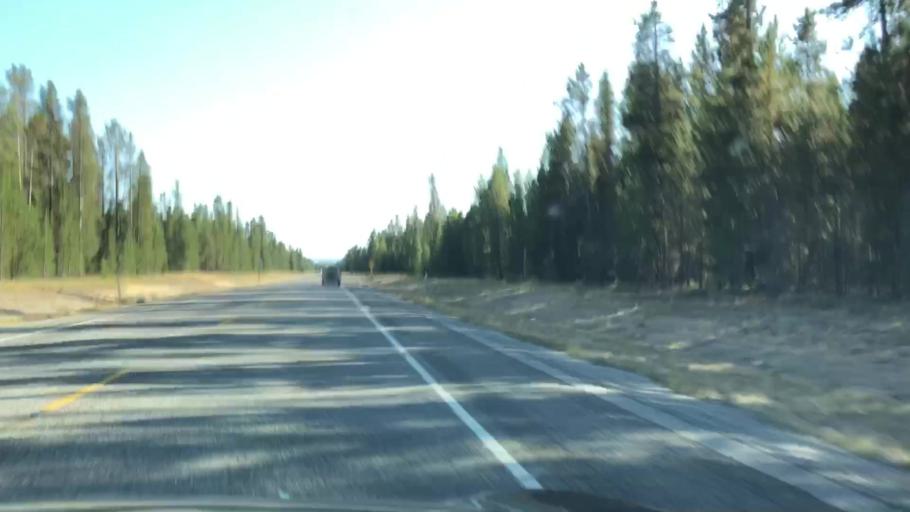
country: US
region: Montana
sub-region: Gallatin County
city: West Yellowstone
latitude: 44.7506
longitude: -111.1134
